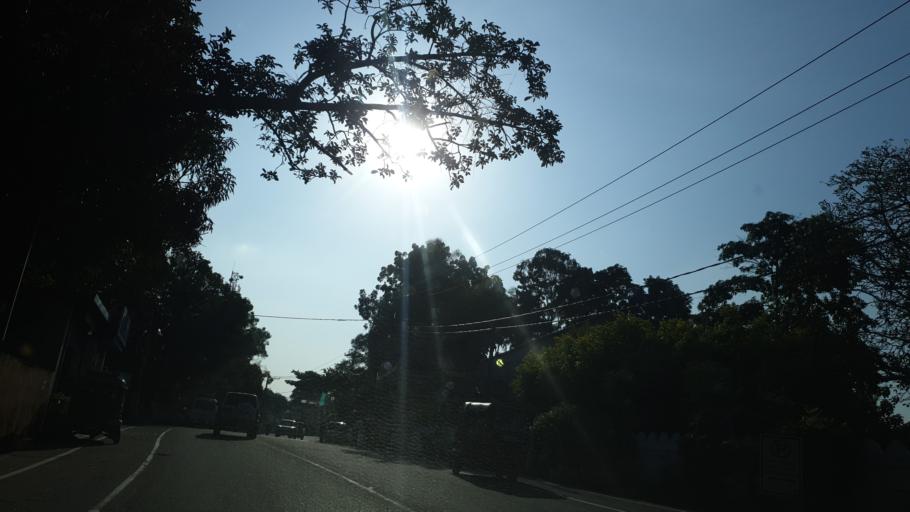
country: LK
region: Western
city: Sri Jayewardenepura Kotte
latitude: 6.8564
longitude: 79.8891
